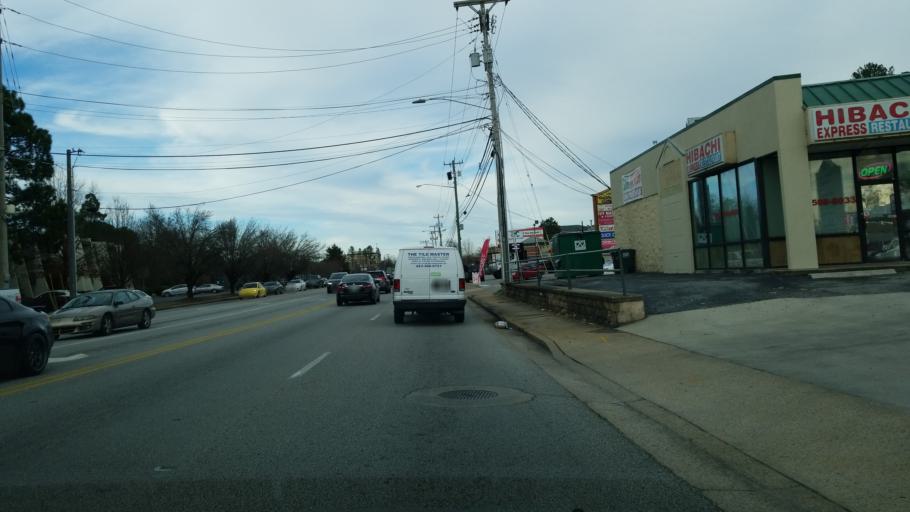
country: US
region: Tennessee
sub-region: Hamilton County
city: East Brainerd
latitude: 35.0154
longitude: -85.1635
